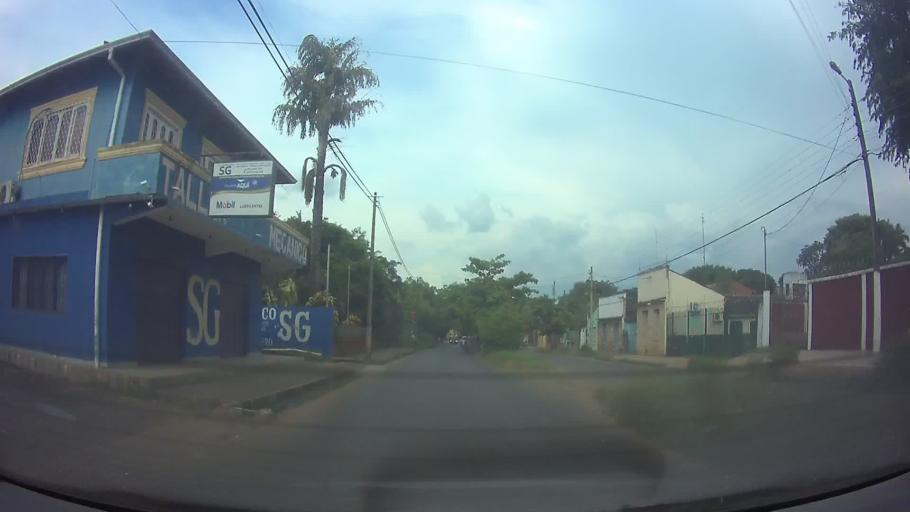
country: PY
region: Central
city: San Lorenzo
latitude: -25.2714
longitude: -57.4813
